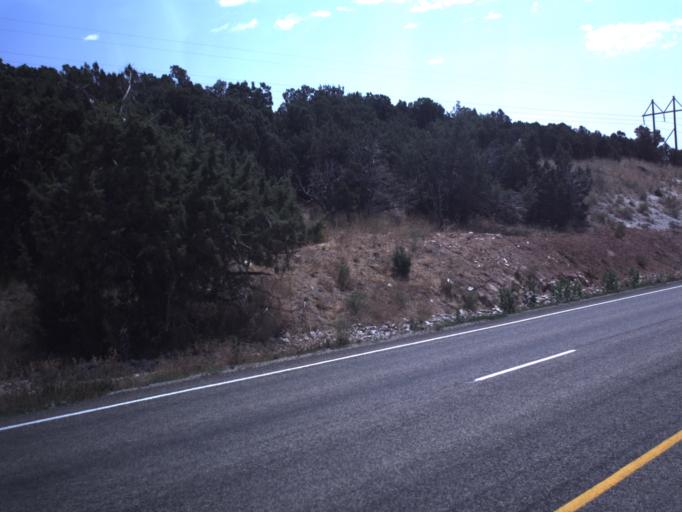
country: US
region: Utah
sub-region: Uintah County
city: Vernal
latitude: 40.6270
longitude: -109.4753
